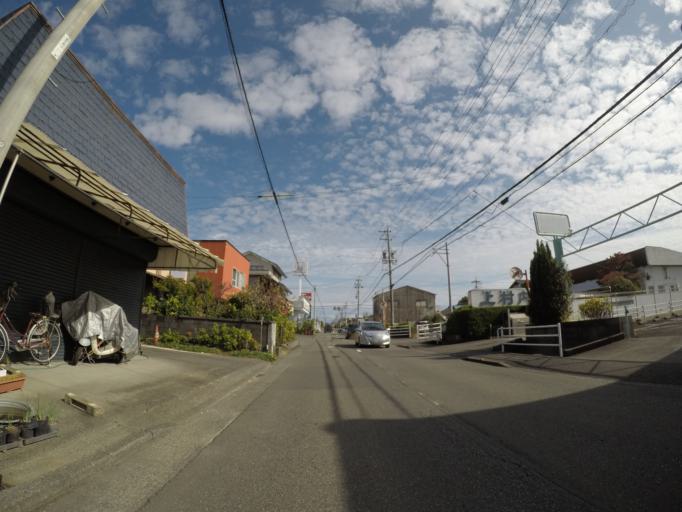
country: JP
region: Shizuoka
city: Fujieda
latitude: 34.8588
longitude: 138.2912
